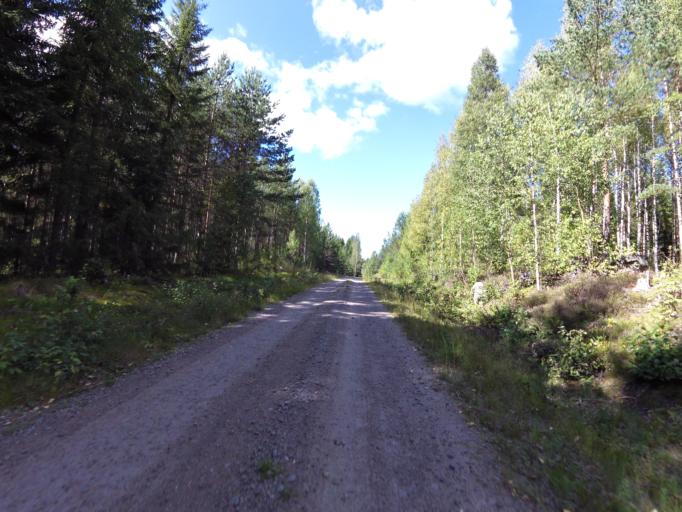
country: SE
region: Gaevleborg
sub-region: Ockelbo Kommun
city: Ockelbo
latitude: 60.8042
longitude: 16.8086
